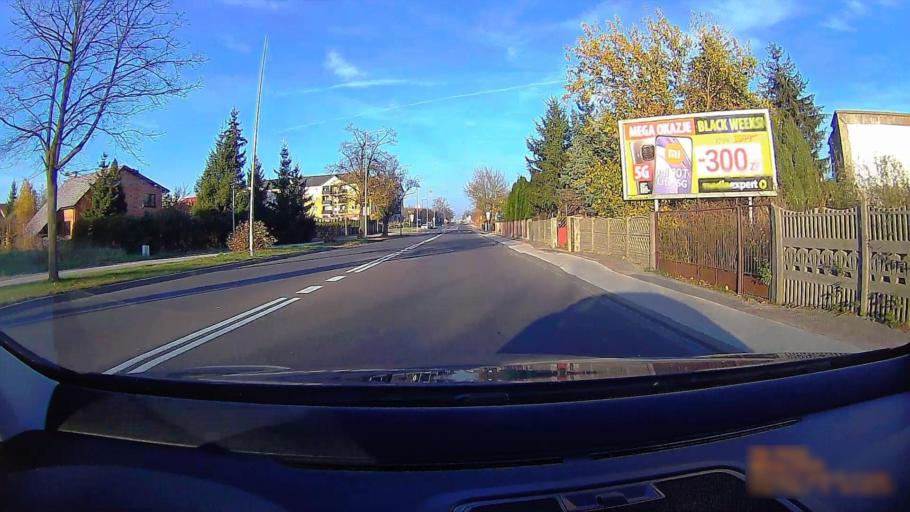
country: PL
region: Greater Poland Voivodeship
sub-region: Powiat koninski
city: Stare Miasto
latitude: 52.1928
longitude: 18.2351
